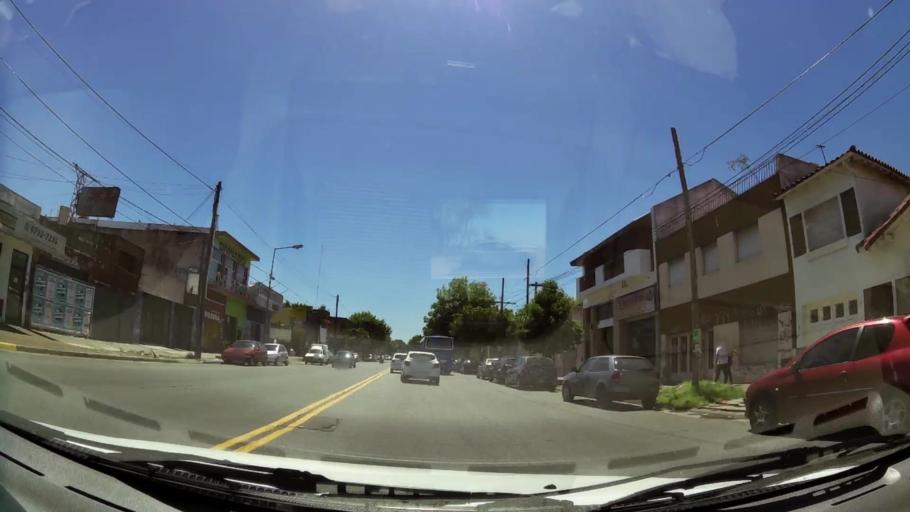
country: AR
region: Buenos Aires
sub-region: Partido de General San Martin
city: General San Martin
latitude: -34.5712
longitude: -58.5422
